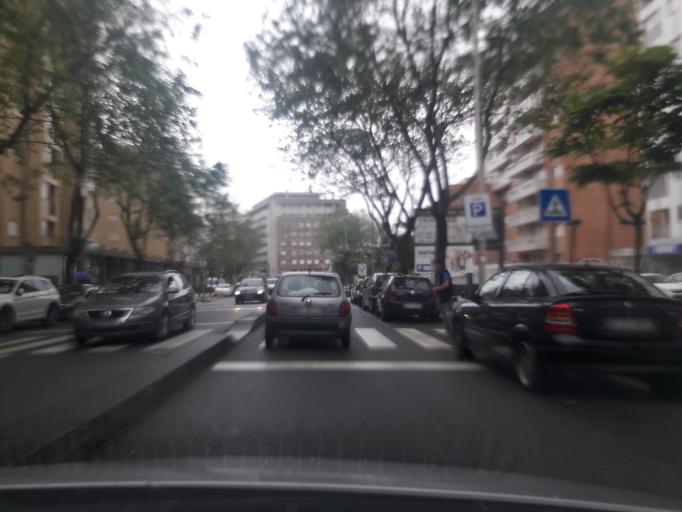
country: PT
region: Porto
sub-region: Povoa de Varzim
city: Povoa de Varzim
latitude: 41.3882
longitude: -8.7670
